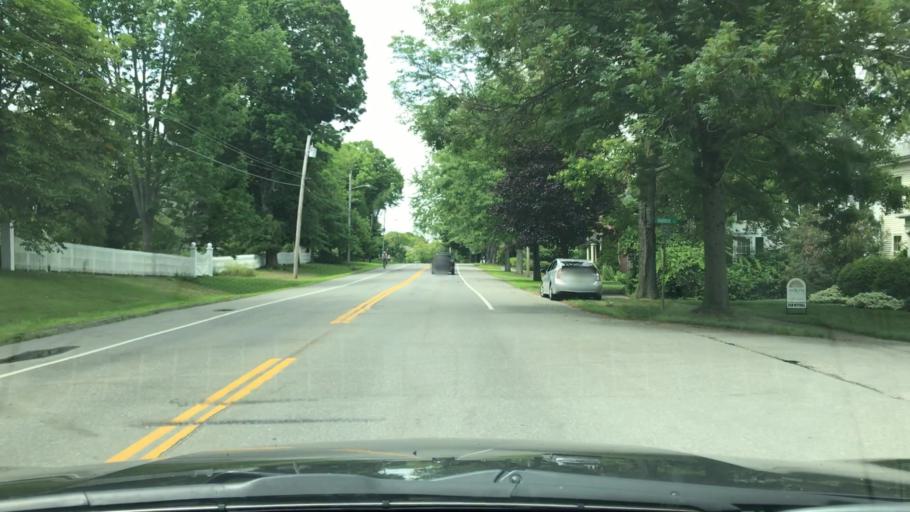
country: US
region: Maine
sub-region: Waldo County
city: Belfast
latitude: 44.4213
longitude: -69.0001
